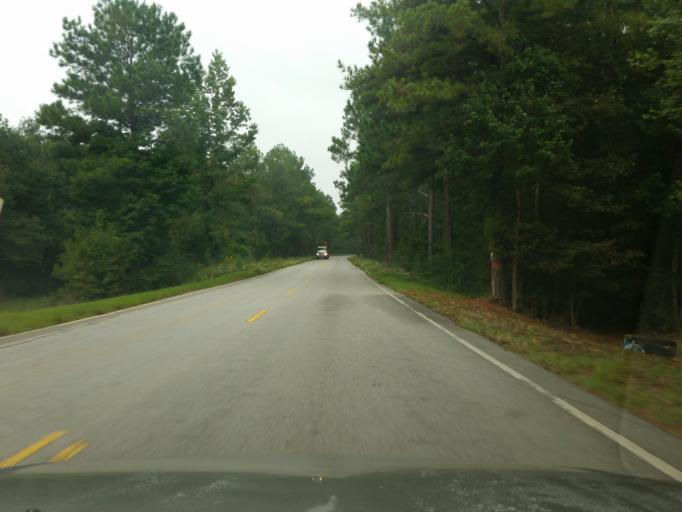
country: US
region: Florida
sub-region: Escambia County
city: Cantonment
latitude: 30.5998
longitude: -87.3962
